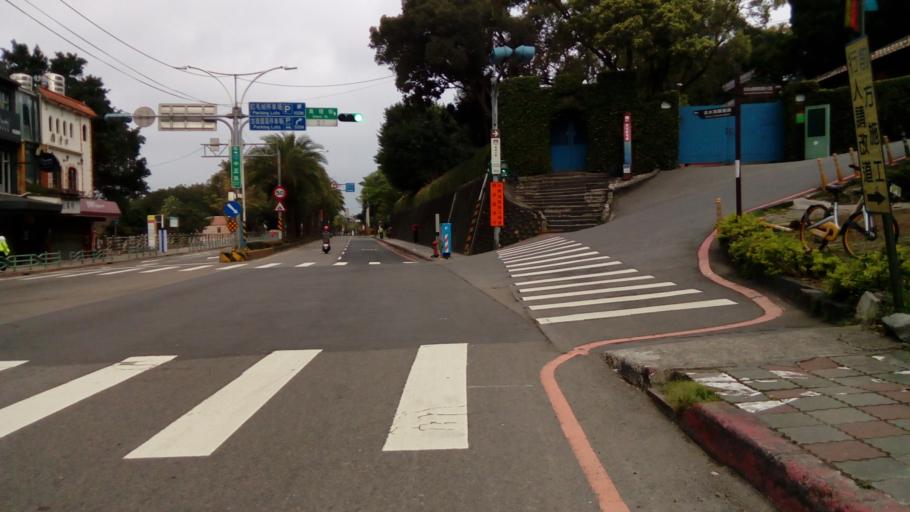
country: TW
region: Taipei
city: Taipei
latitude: 25.1744
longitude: 121.4339
